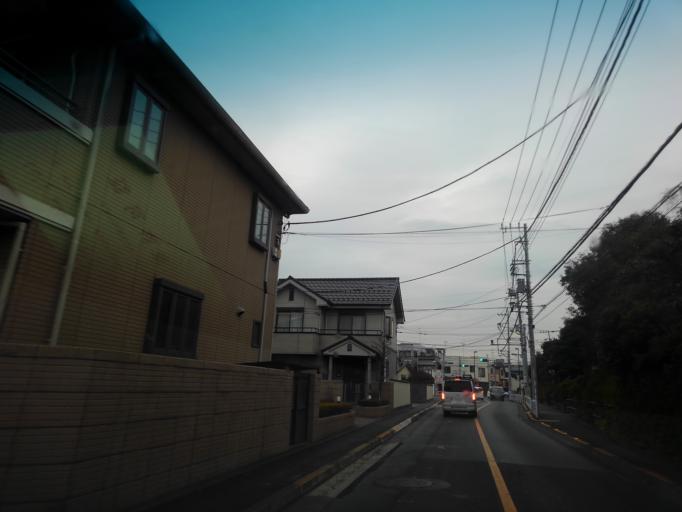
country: JP
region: Tokyo
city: Kokubunji
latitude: 35.7085
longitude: 139.4491
